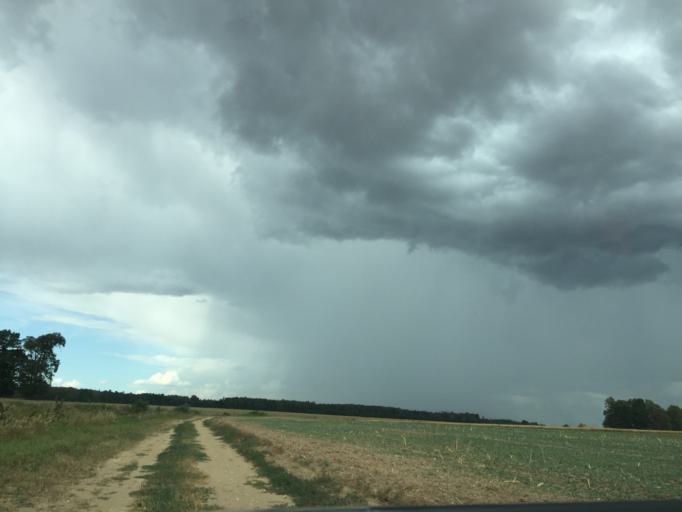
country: LT
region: Siauliu apskritis
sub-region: Joniskis
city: Joniskis
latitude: 56.2903
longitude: 23.7260
